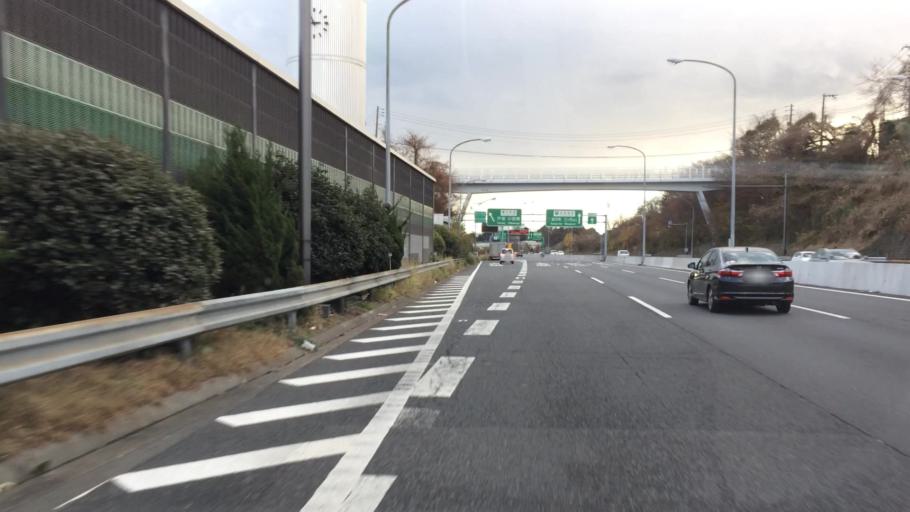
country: JP
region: Kanagawa
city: Yokohama
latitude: 35.4823
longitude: 139.5945
